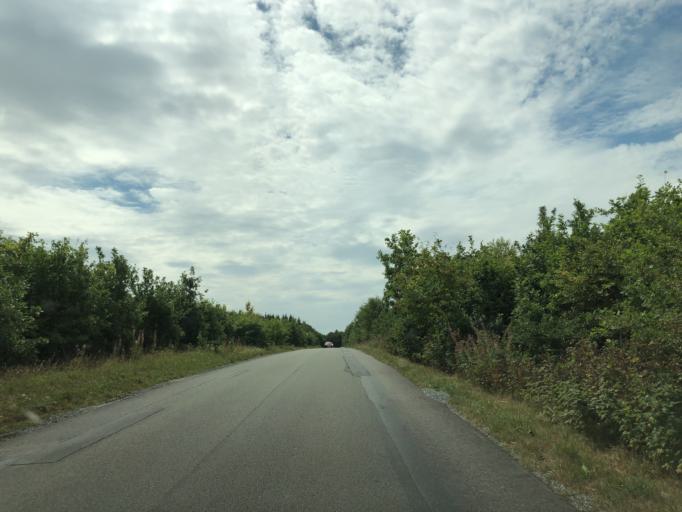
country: DK
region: South Denmark
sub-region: Vejle Kommune
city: Egtved
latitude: 55.6300
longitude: 9.1951
